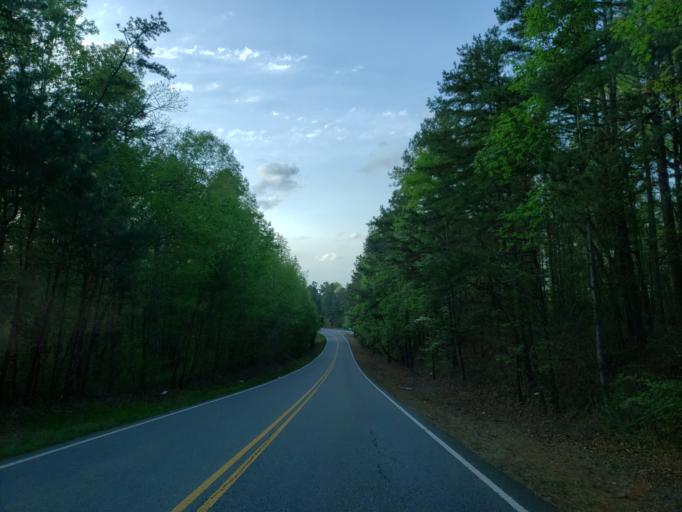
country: US
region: Georgia
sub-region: Cherokee County
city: Ball Ground
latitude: 34.2735
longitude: -84.3716
